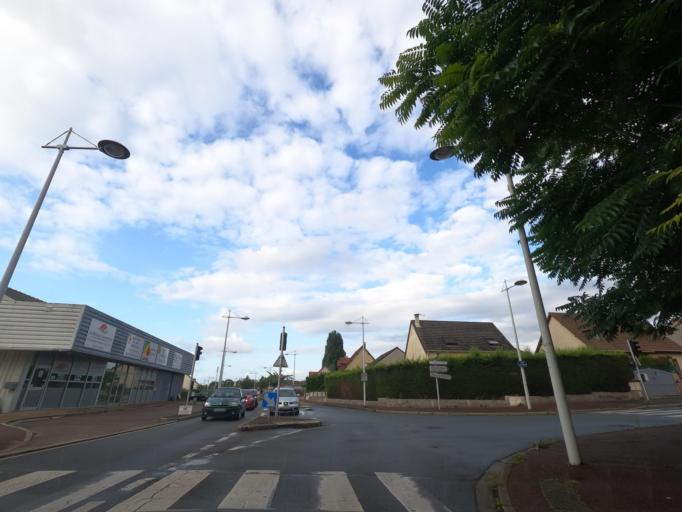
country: FR
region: Haute-Normandie
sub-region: Departement de la Seine-Maritime
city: Grand-Couronne
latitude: 49.3614
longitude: 1.0121
